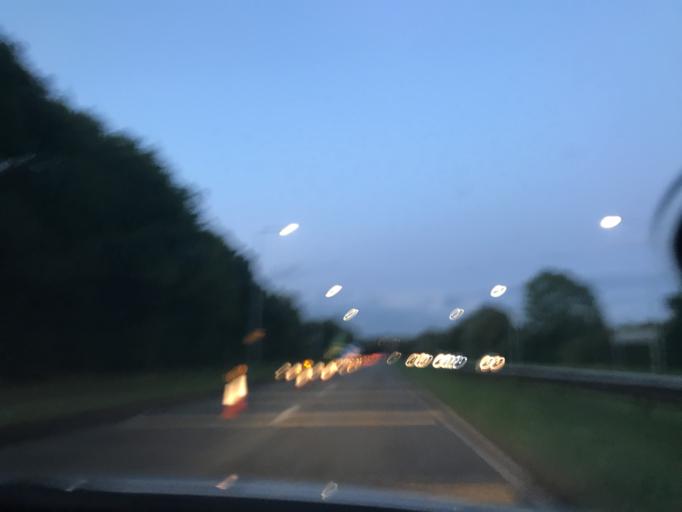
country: GB
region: England
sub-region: Cheshire West and Chester
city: Northwich
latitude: 53.2372
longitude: -2.5188
